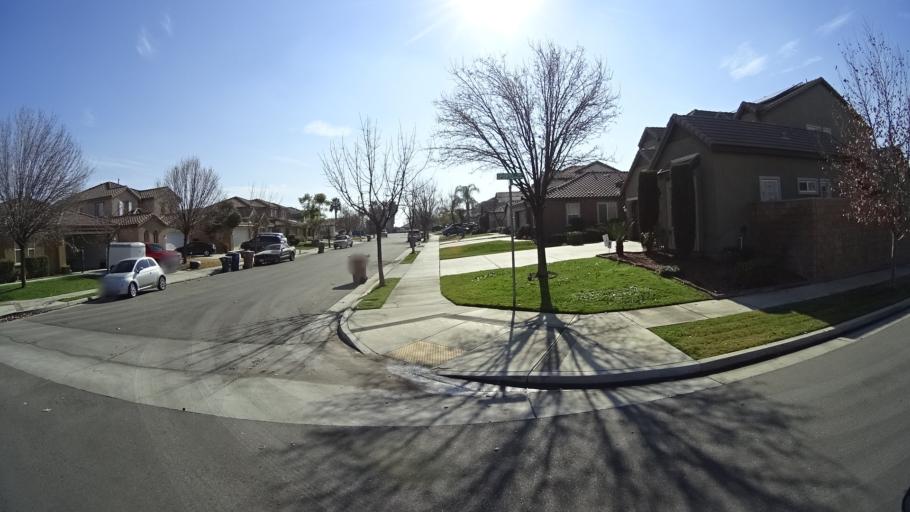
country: US
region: California
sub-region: Kern County
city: Oildale
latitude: 35.4056
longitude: -118.8930
